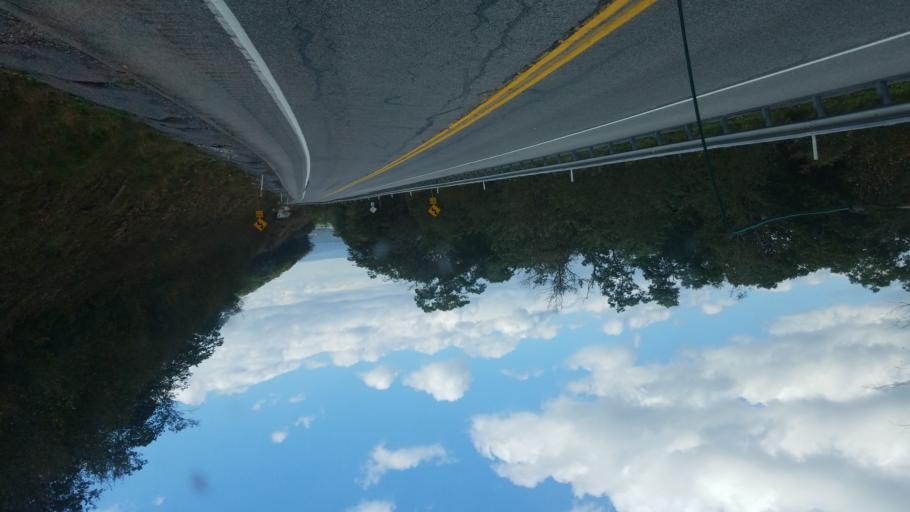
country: US
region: Pennsylvania
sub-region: Fulton County
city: McConnellsburg
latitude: 40.0148
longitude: -78.1391
